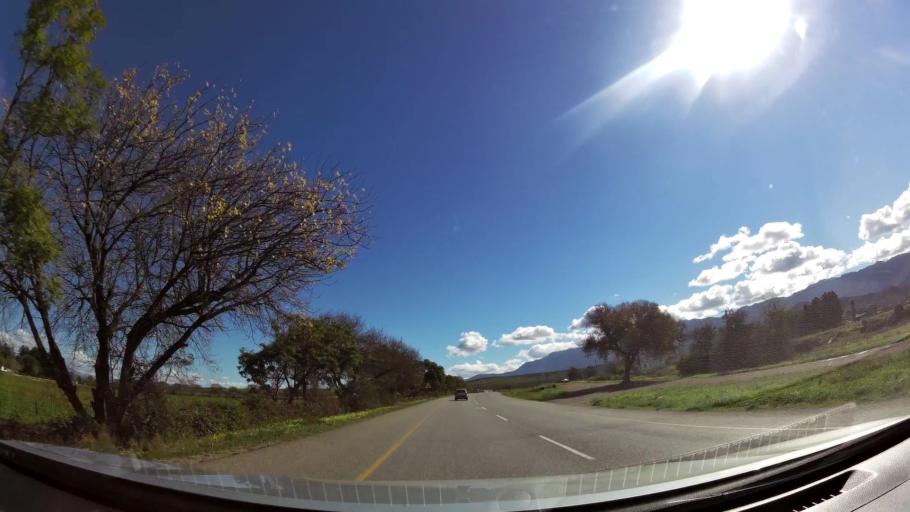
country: ZA
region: Western Cape
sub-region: Cape Winelands District Municipality
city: Ashton
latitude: -33.8248
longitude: 19.9800
